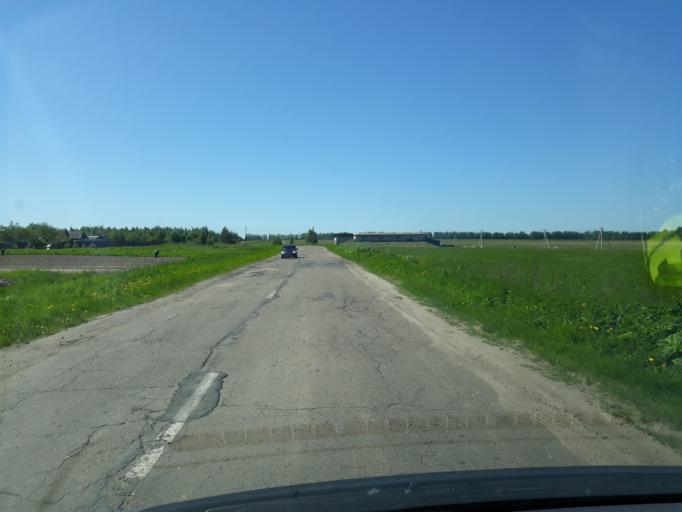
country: RU
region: Jaroslavl
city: Yaroslavl
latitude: 57.6806
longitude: 40.0134
